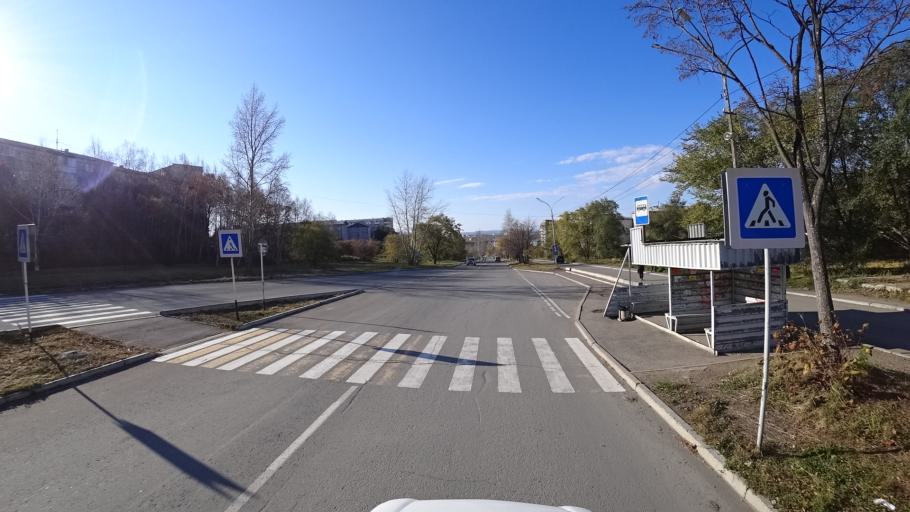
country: RU
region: Khabarovsk Krai
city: Amursk
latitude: 50.2419
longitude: 136.9135
